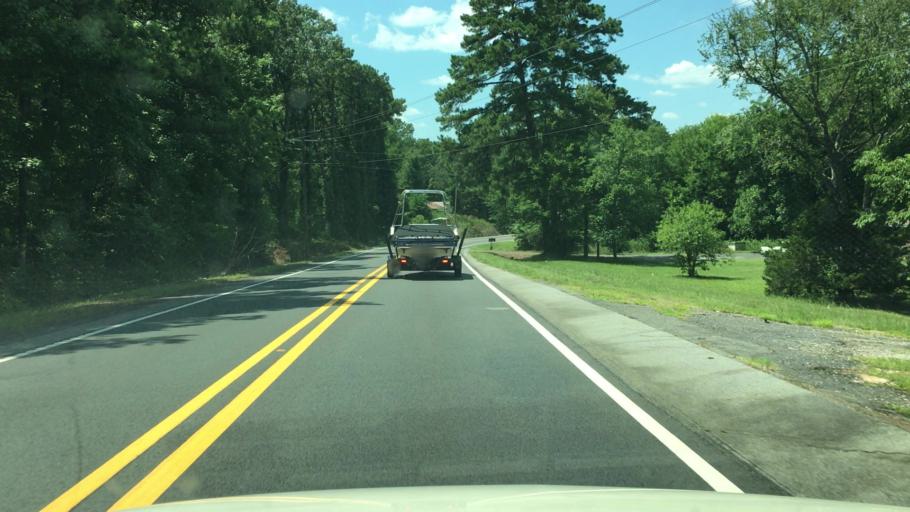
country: US
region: Arkansas
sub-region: Clark County
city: Arkadelphia
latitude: 34.2495
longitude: -93.1183
